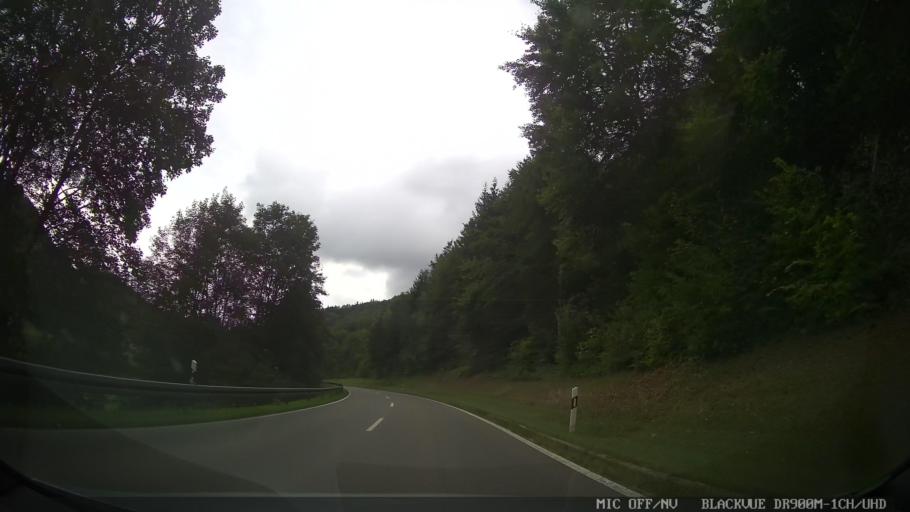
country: DE
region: Baden-Wuerttemberg
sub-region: Freiburg Region
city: Barenthal
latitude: 48.0465
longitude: 8.9283
